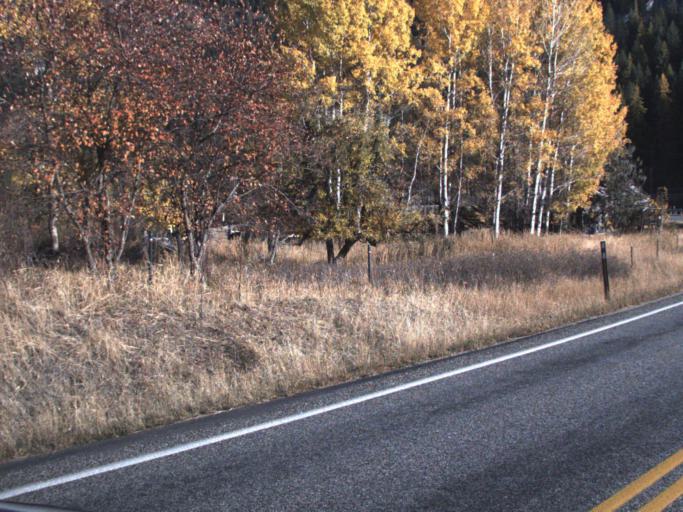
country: CA
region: British Columbia
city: Rossland
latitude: 48.8715
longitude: -117.8456
